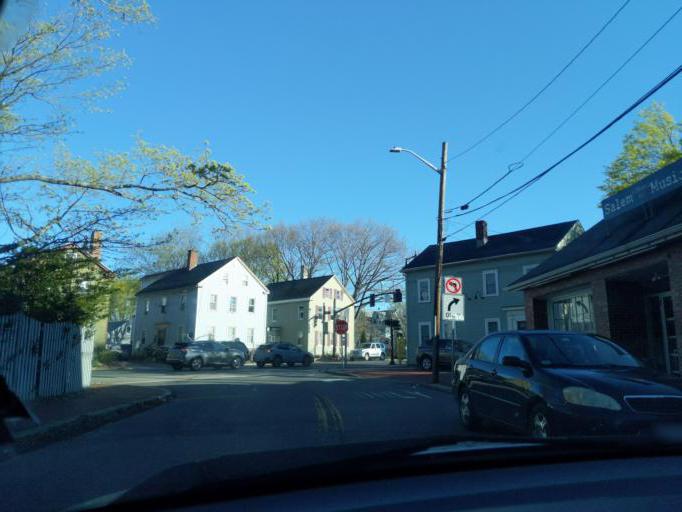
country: US
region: Massachusetts
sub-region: Essex County
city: Salem
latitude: 42.5278
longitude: -70.8901
